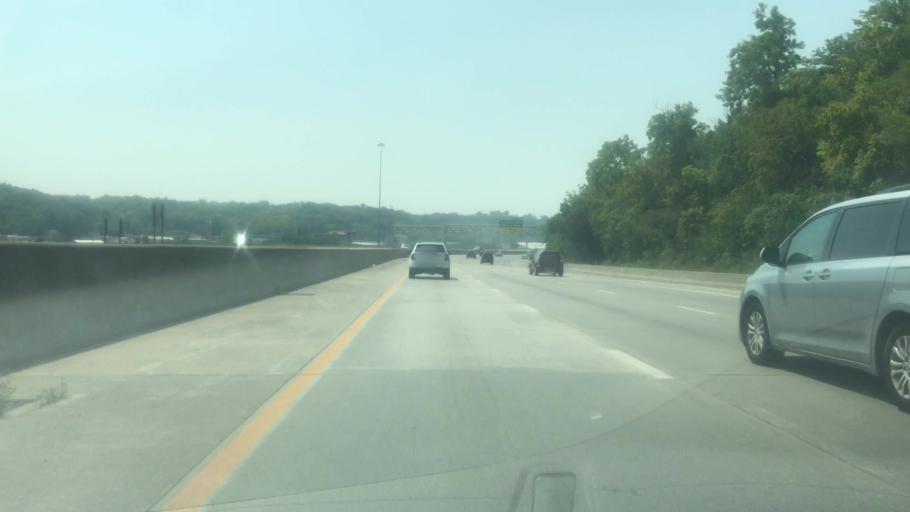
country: US
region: Kansas
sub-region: Johnson County
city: Westwood
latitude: 39.0700
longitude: -94.6196
